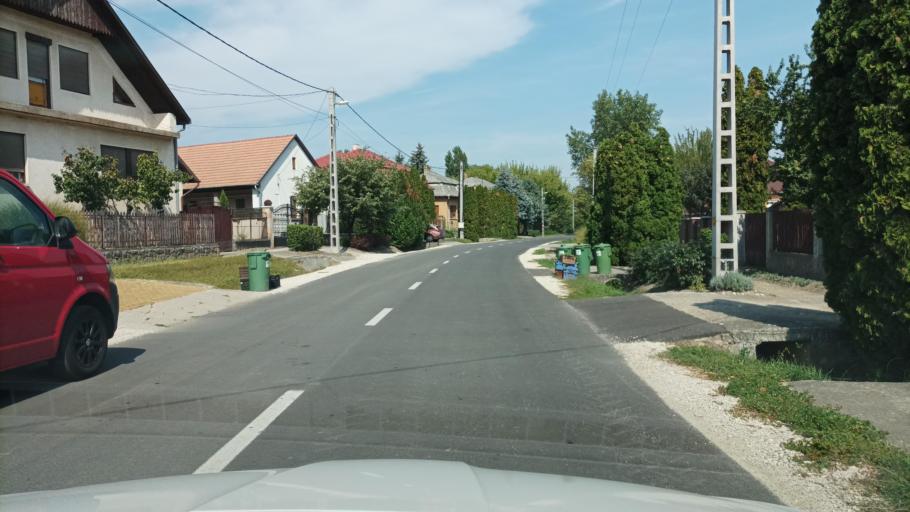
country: HU
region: Pest
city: Galgaheviz
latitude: 47.6241
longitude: 19.5522
